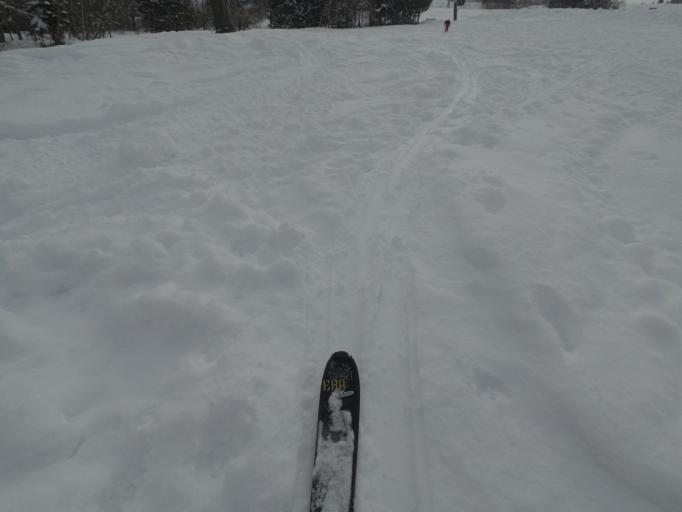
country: AT
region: Salzburg
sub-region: Politischer Bezirk Sankt Johann im Pongau
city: Sankt Johann im Pongau
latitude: 47.3226
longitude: 13.2004
